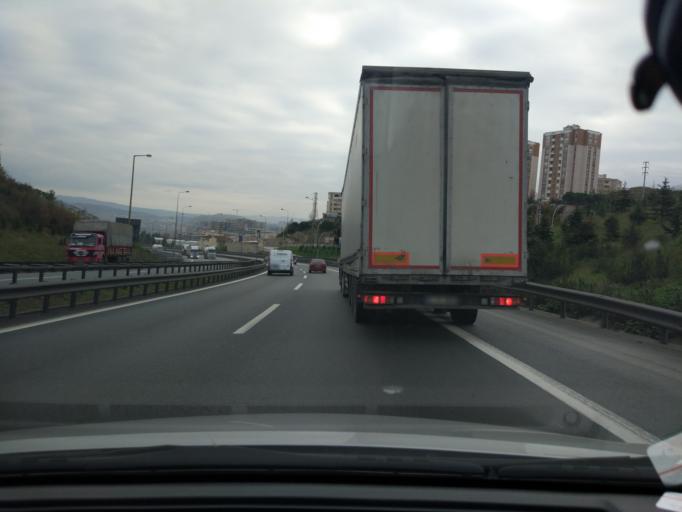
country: TR
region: Kocaeli
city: Izmit
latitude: 40.7825
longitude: 29.9379
